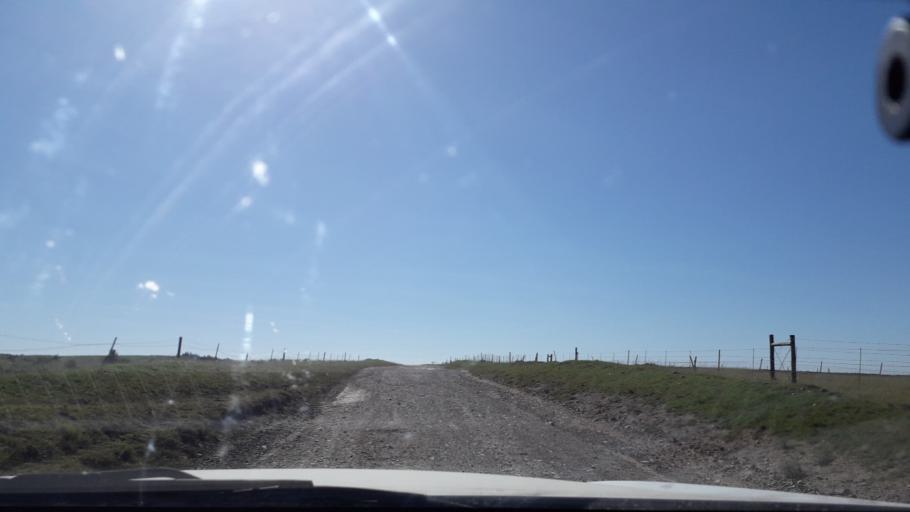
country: ZA
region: Eastern Cape
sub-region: Buffalo City Metropolitan Municipality
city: East London
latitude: -32.8000
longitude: 27.9504
